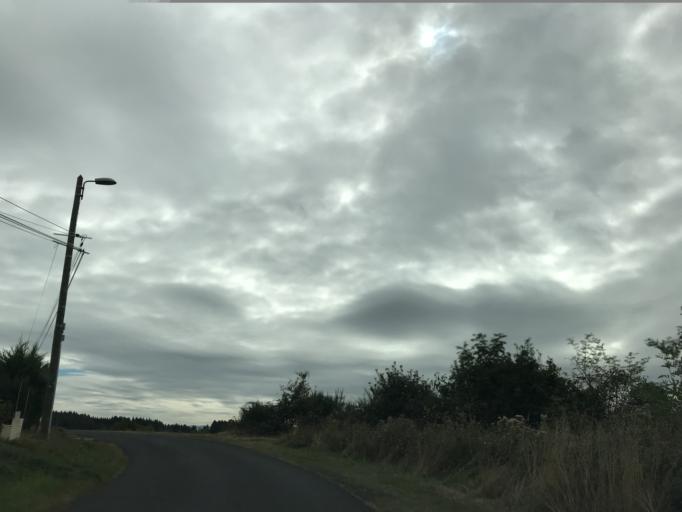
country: FR
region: Auvergne
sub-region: Departement du Puy-de-Dome
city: Escoutoux
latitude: 45.8283
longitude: 3.5799
